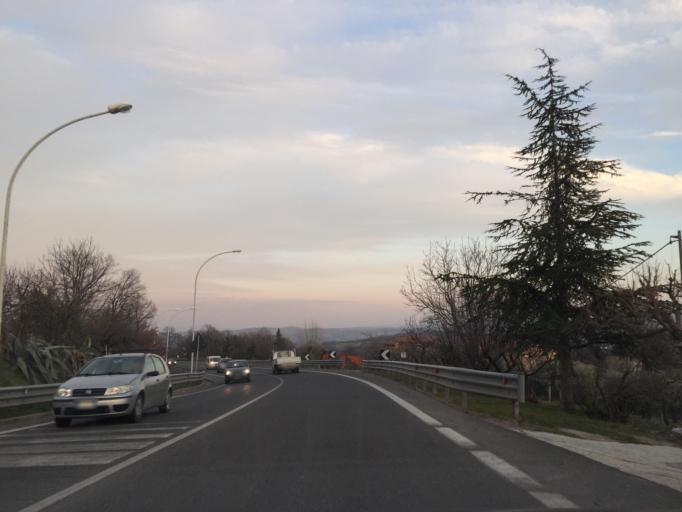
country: IT
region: Molise
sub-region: Provincia di Campobasso
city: Campobasso
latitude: 41.5606
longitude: 14.6893
